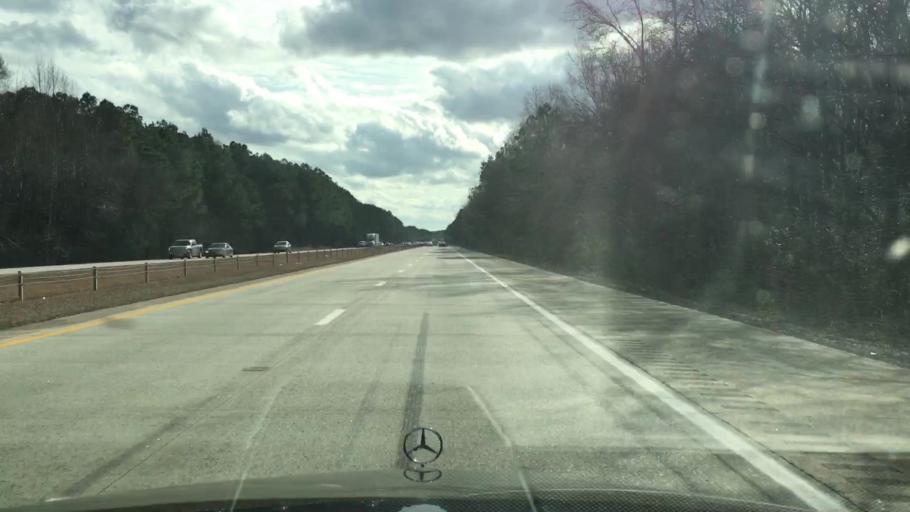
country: US
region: North Carolina
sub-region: Johnston County
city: Benson
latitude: 35.4995
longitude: -78.5541
